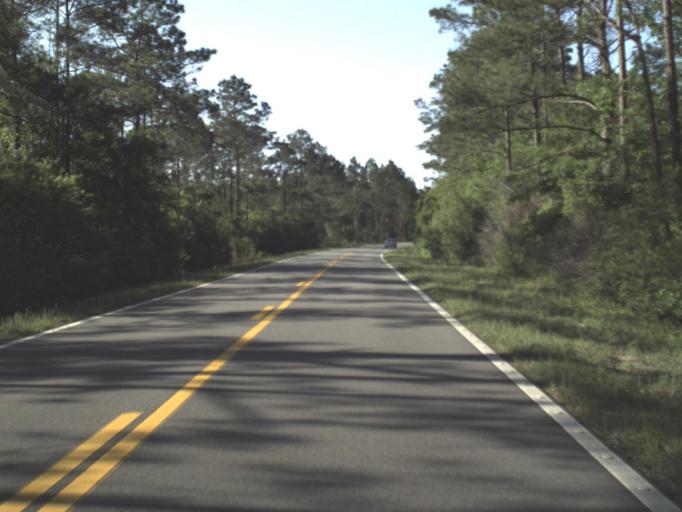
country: US
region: Florida
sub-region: Gulf County
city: Wewahitchka
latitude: 30.1268
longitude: -84.9893
